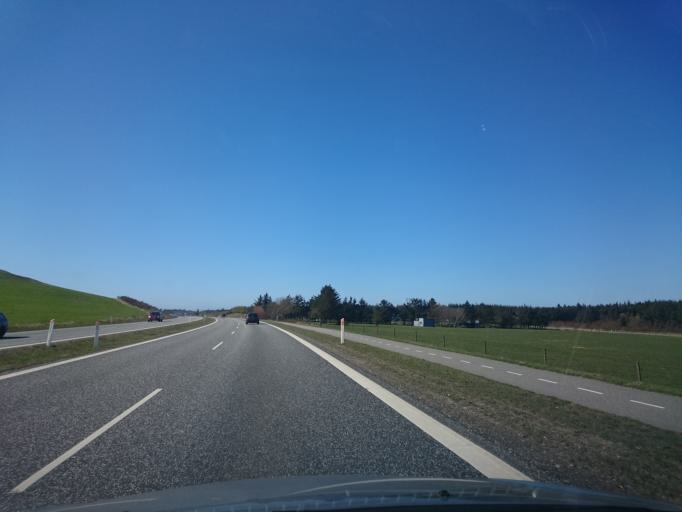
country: DK
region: North Denmark
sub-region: Hjorring Kommune
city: Hirtshals
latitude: 57.5702
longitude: 10.0088
